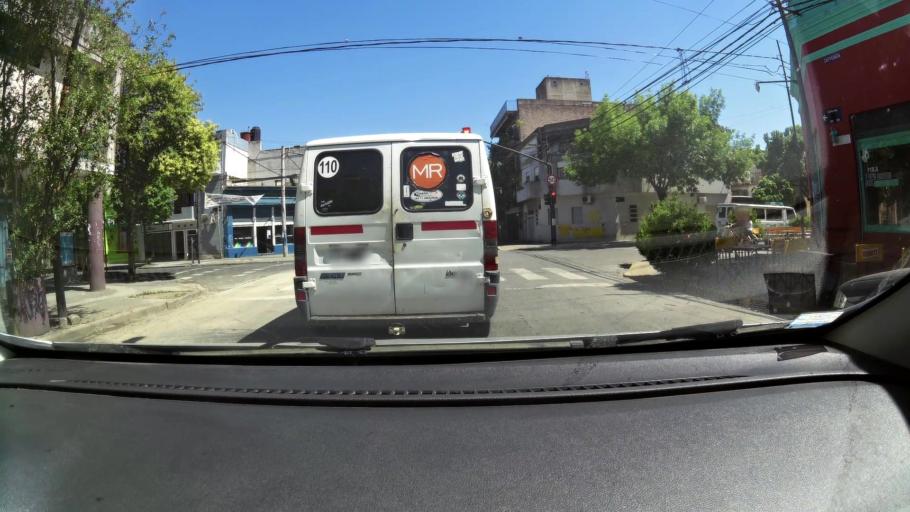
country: AR
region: Santa Fe
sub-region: Departamento de Rosario
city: Rosario
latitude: -32.9346
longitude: -60.6694
